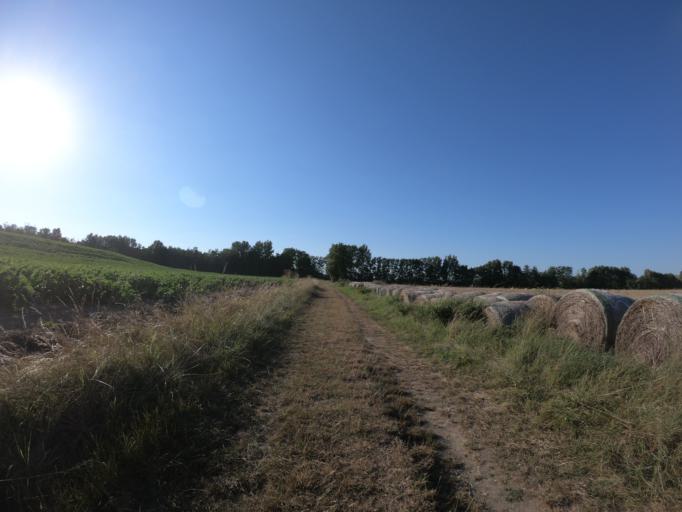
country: FR
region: Midi-Pyrenees
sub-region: Departement de l'Ariege
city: La Tour-du-Crieu
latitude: 43.1047
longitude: 1.7291
